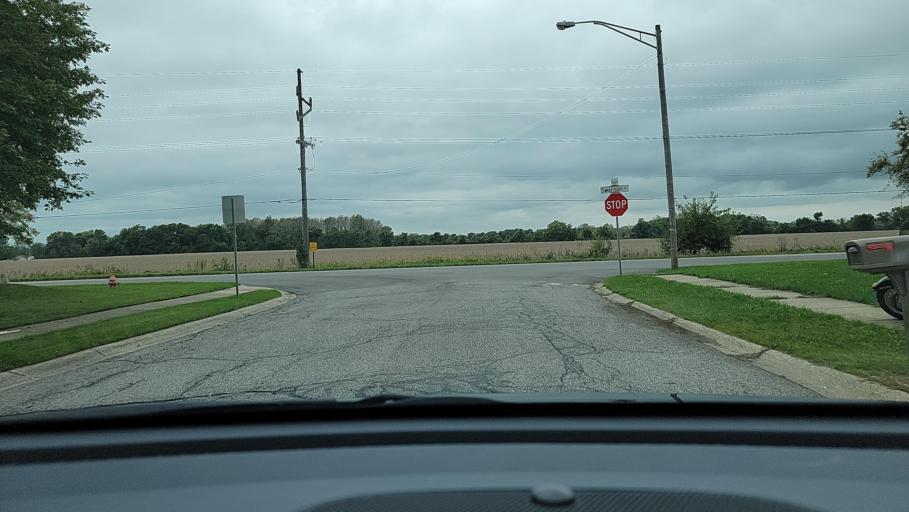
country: US
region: Indiana
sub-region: Porter County
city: Portage
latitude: 41.5451
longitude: -87.1967
